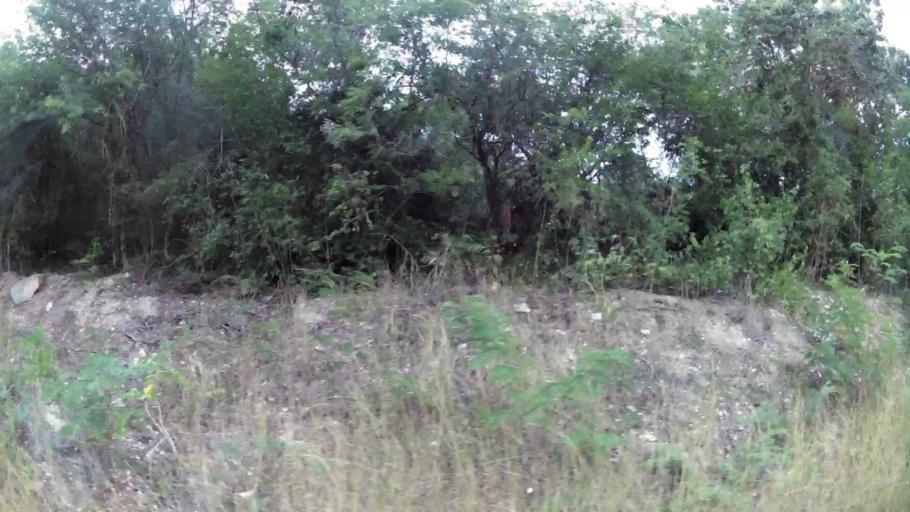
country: AG
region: Saint John
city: Potters Village
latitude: 17.0865
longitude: -61.8082
